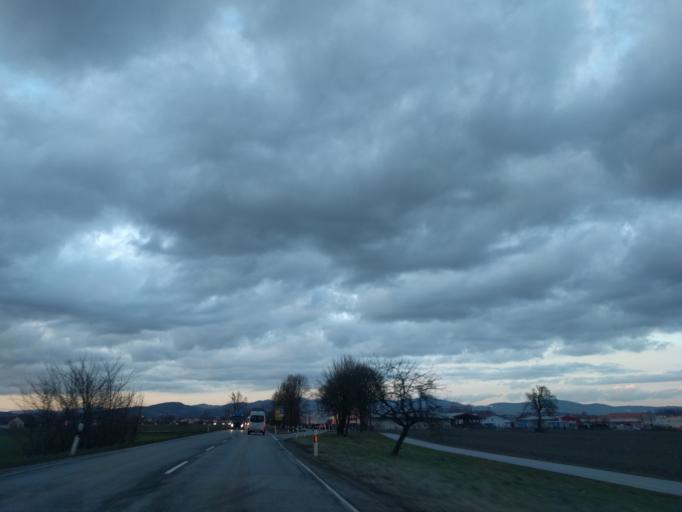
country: DE
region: Bavaria
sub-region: Lower Bavaria
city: Hengersberg
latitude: 48.7571
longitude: 13.0534
